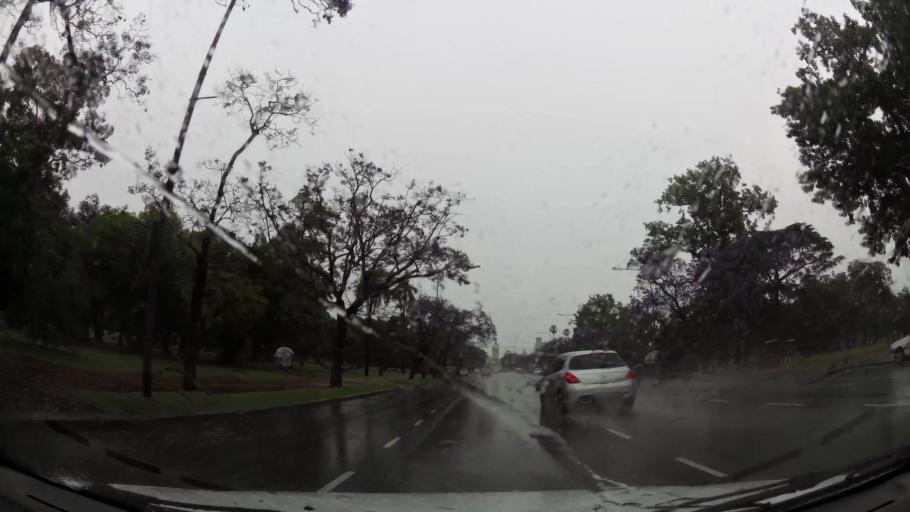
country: AR
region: Buenos Aires F.D.
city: Retiro
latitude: -34.5728
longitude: -58.4129
